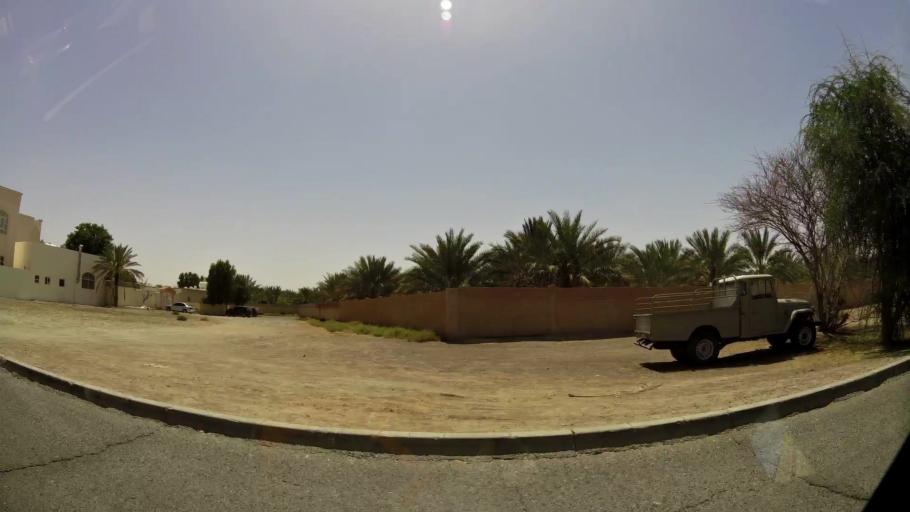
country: OM
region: Al Buraimi
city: Al Buraymi
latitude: 24.2779
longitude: 55.7759
